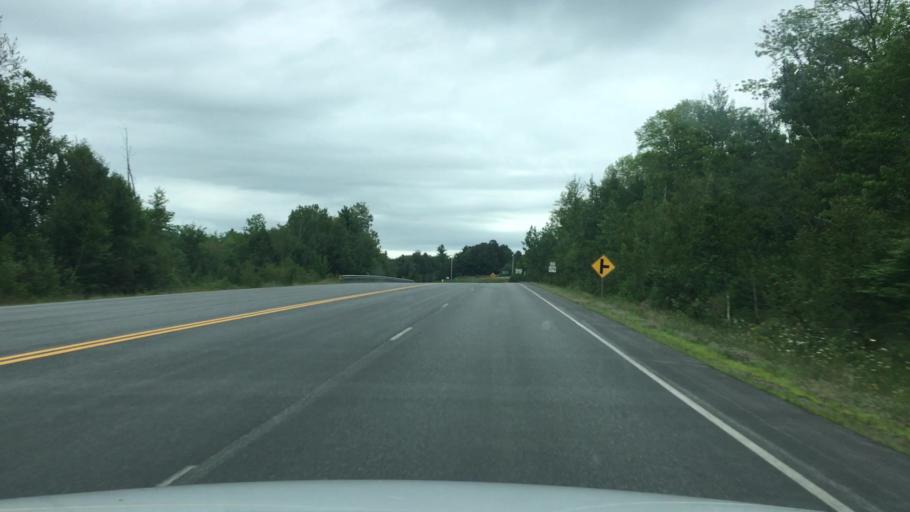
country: US
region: Maine
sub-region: Hancock County
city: Franklin
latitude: 44.8487
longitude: -68.3339
